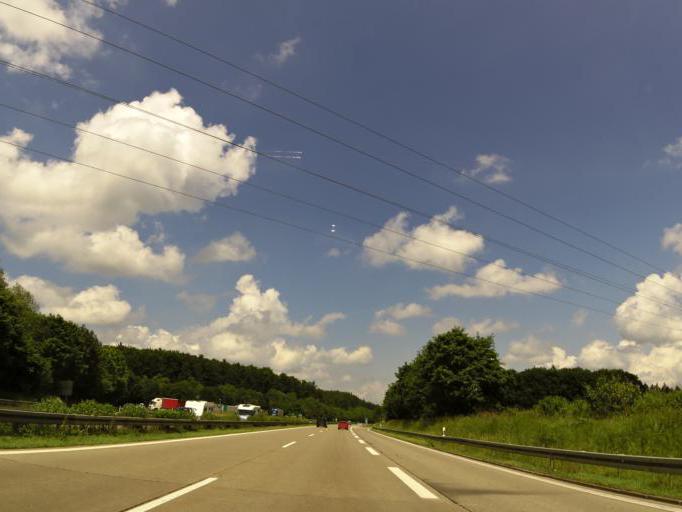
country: DE
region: Baden-Wuerttemberg
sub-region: Regierungsbezirk Stuttgart
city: Nattheim
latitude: 48.7365
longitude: 10.1978
